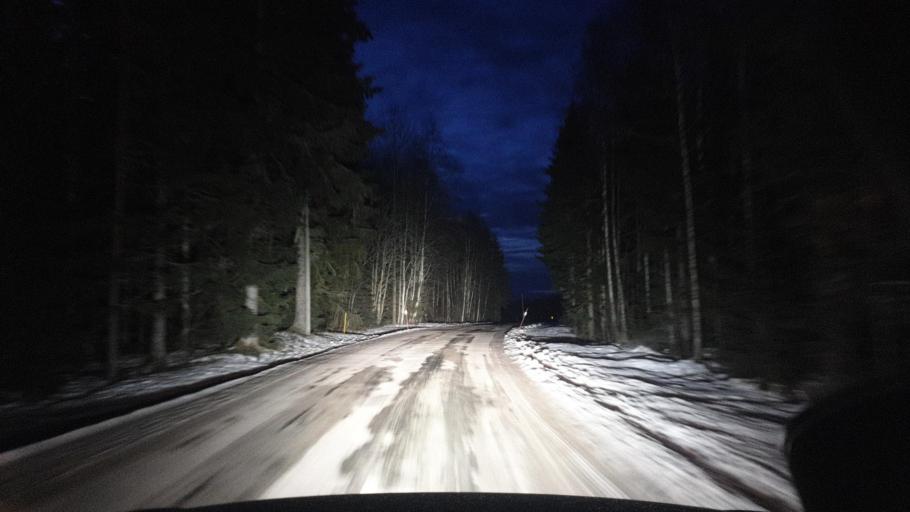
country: SE
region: Vaermland
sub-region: Eda Kommun
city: Charlottenberg
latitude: 59.8599
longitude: 12.3437
